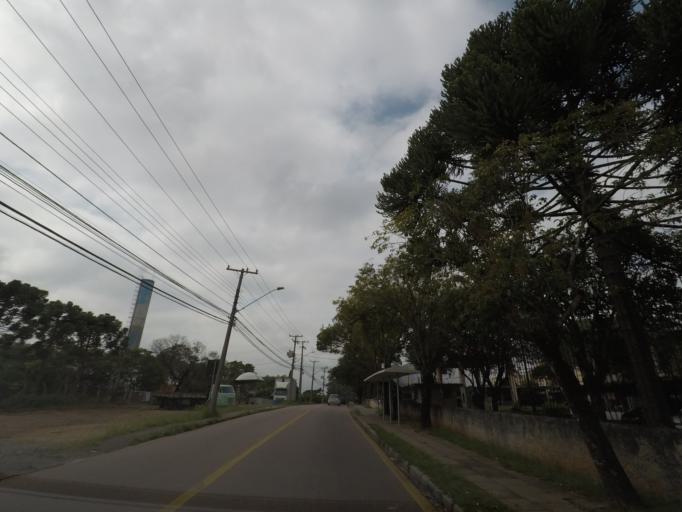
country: BR
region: Parana
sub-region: Curitiba
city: Curitiba
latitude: -25.4945
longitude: -49.3180
